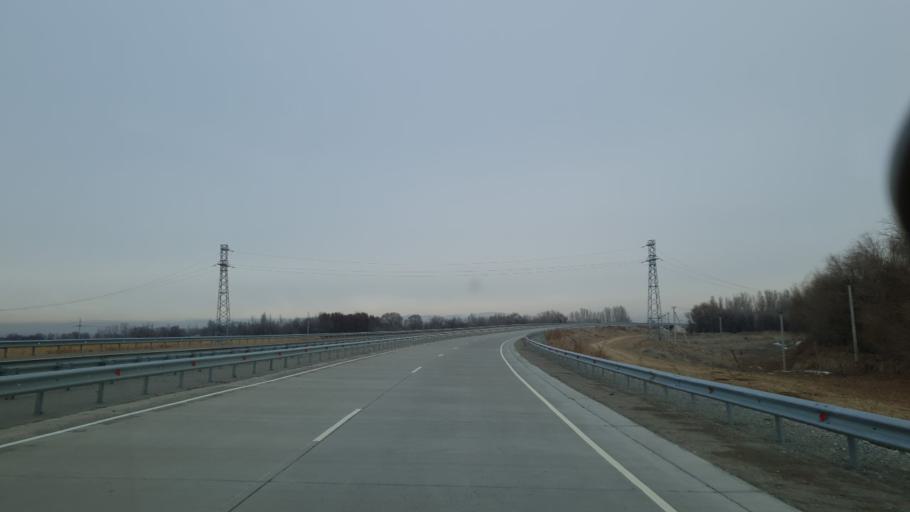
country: KZ
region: Almaty Oblysy
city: Zharkent
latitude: 44.1725
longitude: 80.1594
